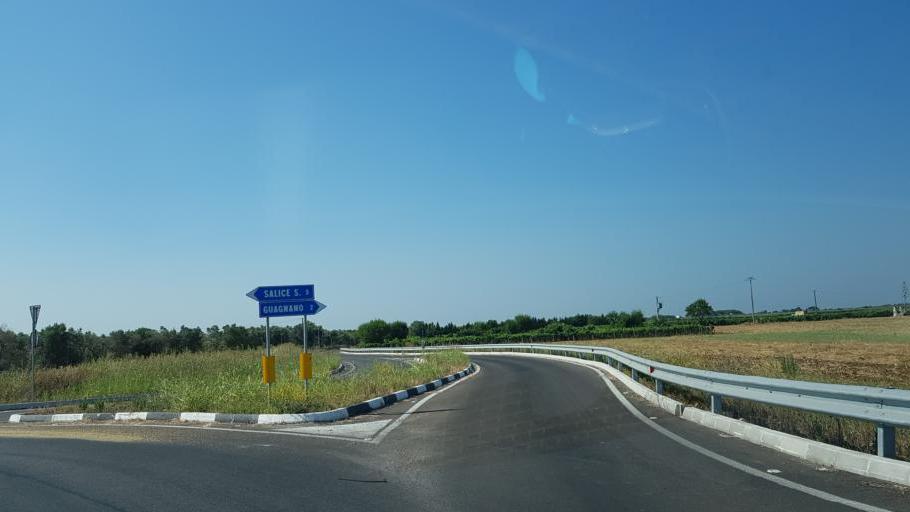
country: IT
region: Apulia
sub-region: Provincia di Lecce
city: Guagnano
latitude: 40.4217
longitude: 17.9497
